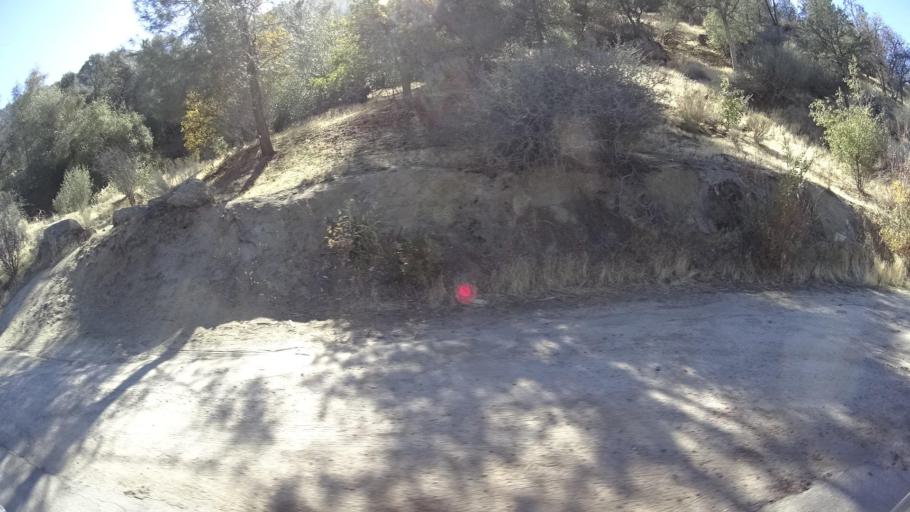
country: US
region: California
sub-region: Kern County
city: Bodfish
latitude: 35.5758
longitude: -118.5532
